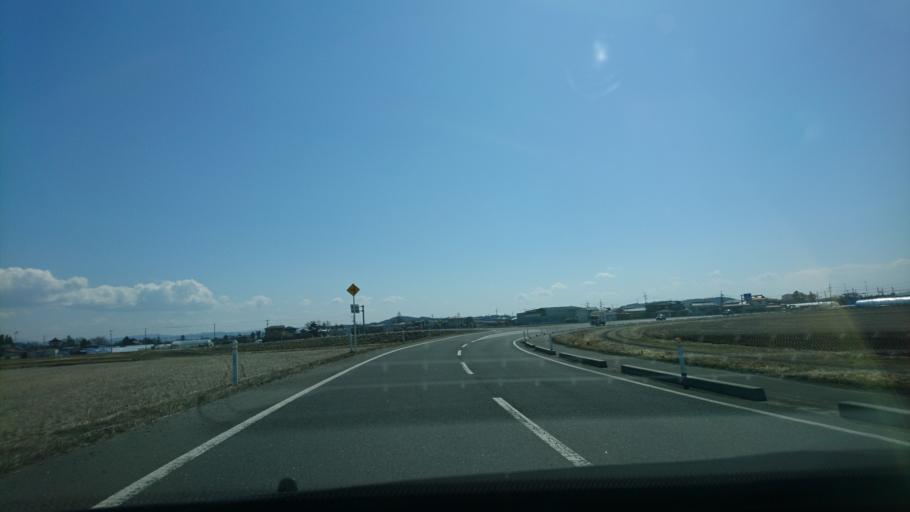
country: JP
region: Iwate
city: Ichinoseki
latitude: 38.7776
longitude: 141.1409
